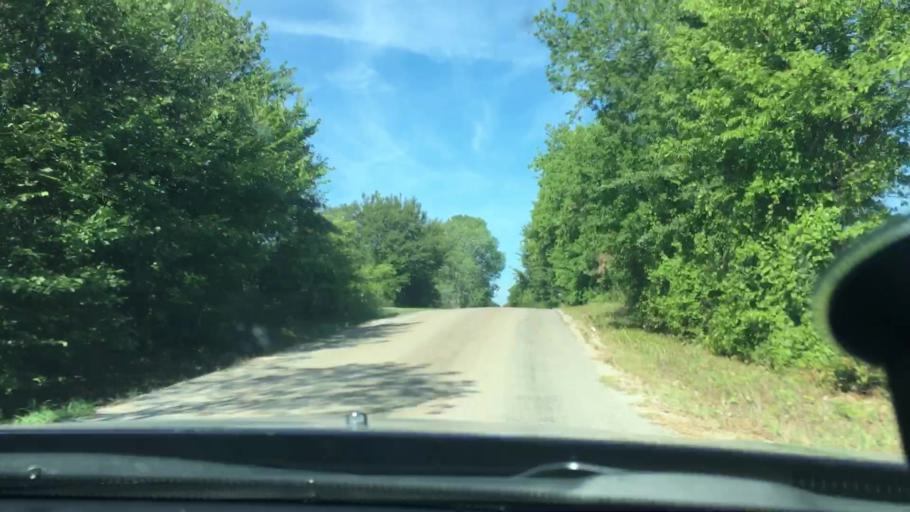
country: US
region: Oklahoma
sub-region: Carter County
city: Lone Grove
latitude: 34.2674
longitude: -97.2738
